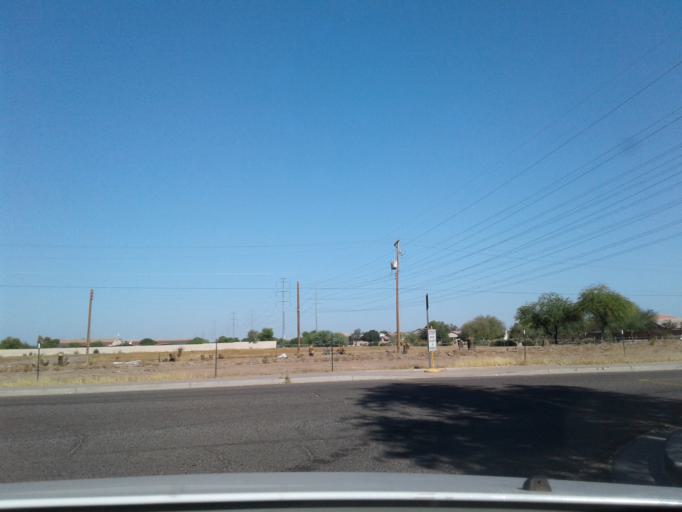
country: US
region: Arizona
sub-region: Maricopa County
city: Laveen
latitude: 33.4150
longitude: -112.1947
